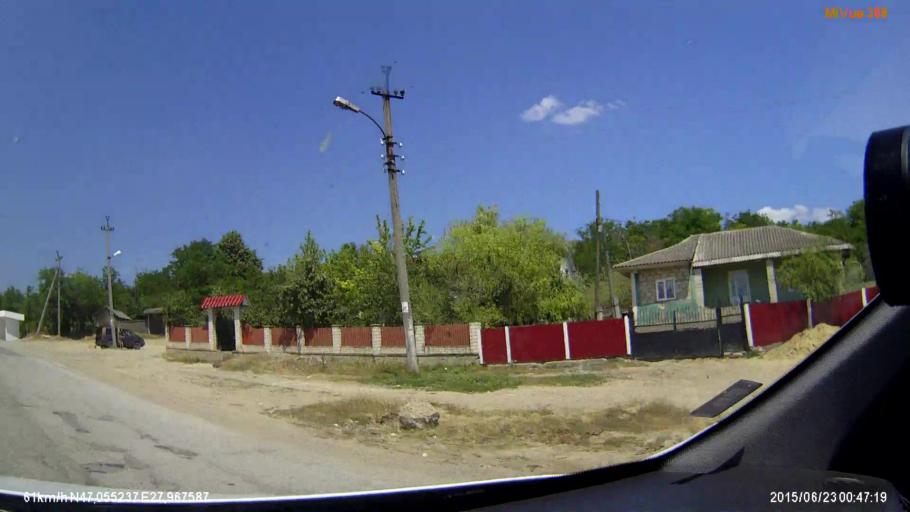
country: RO
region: Iasi
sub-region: Comuna Prisacani
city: Prisacani
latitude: 47.0551
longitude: 27.9676
